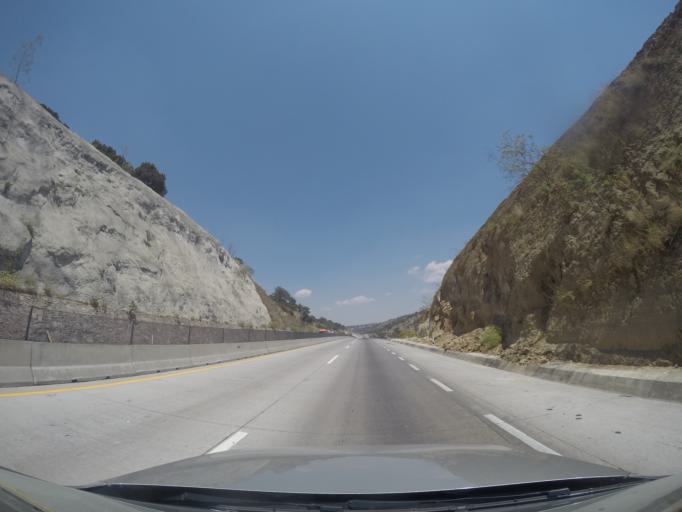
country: MX
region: Tlaxcala
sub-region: Ixtacuixtla de Mariano Matamoros
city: Villa Mariano Matamoros
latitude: 19.3571
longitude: -98.4071
